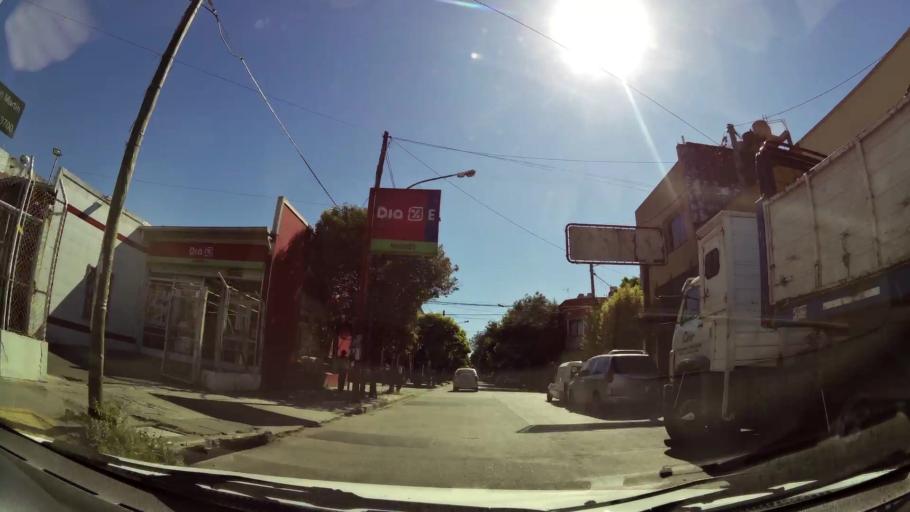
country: AR
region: Buenos Aires
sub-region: Partido de General San Martin
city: General San Martin
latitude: -34.5375
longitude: -58.5117
